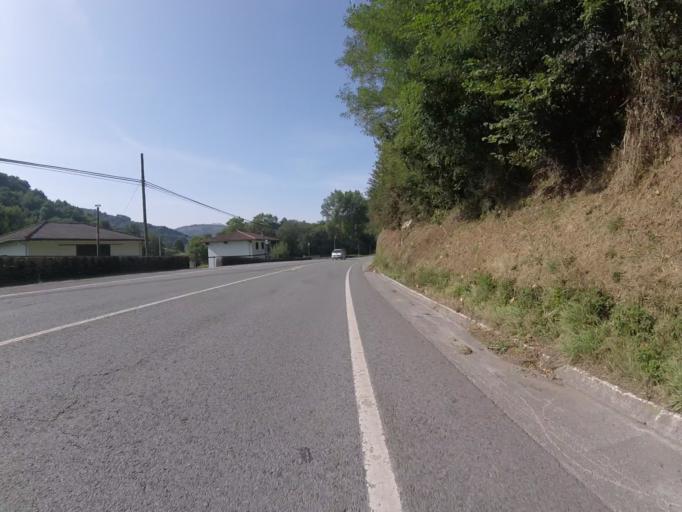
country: ES
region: Navarre
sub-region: Provincia de Navarra
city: Zugarramurdi
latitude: 43.1599
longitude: -1.4981
